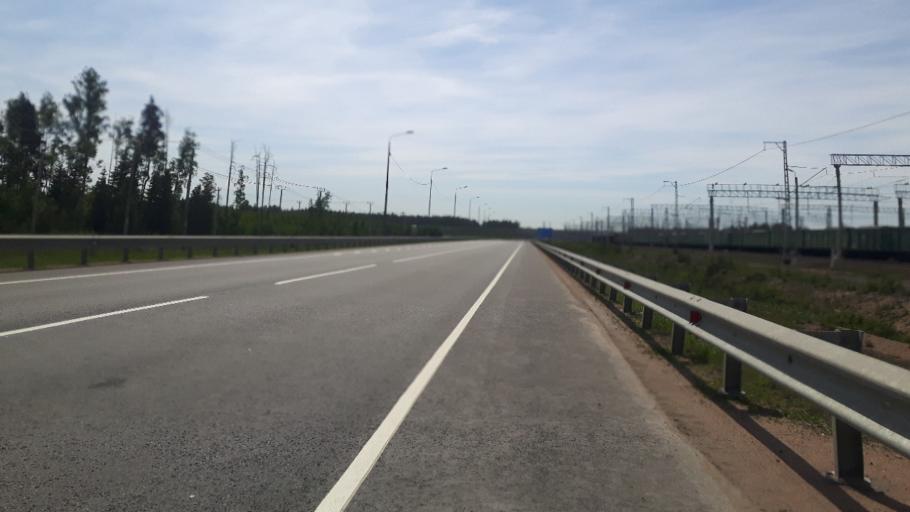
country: RU
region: Leningrad
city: Vistino
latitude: 59.6680
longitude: 28.4332
